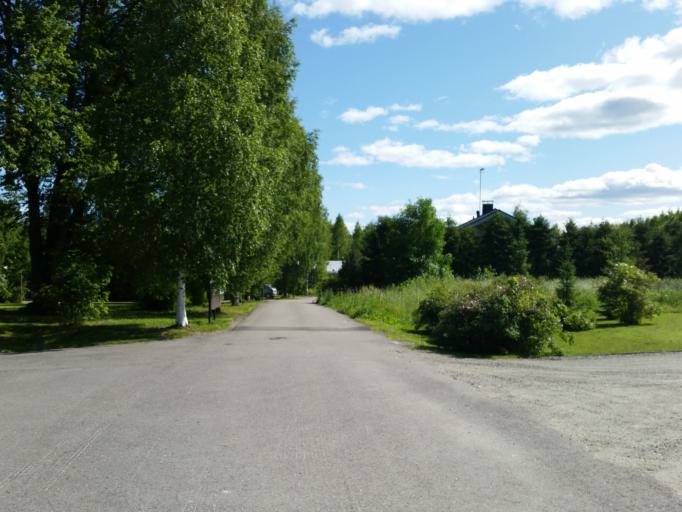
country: FI
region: Northern Savo
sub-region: Varkaus
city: Varkaus
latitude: 62.3367
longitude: 27.9034
